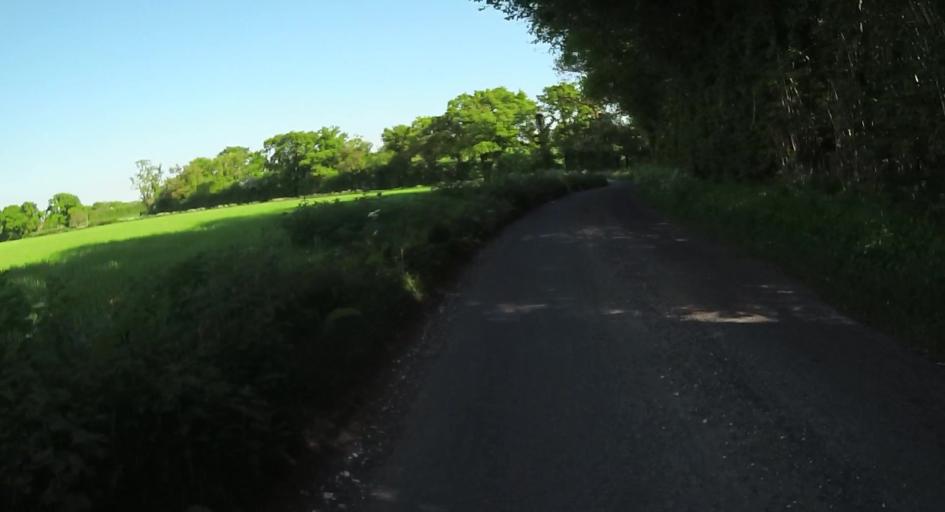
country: GB
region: England
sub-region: Hampshire
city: Overton
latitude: 51.1642
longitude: -1.1861
